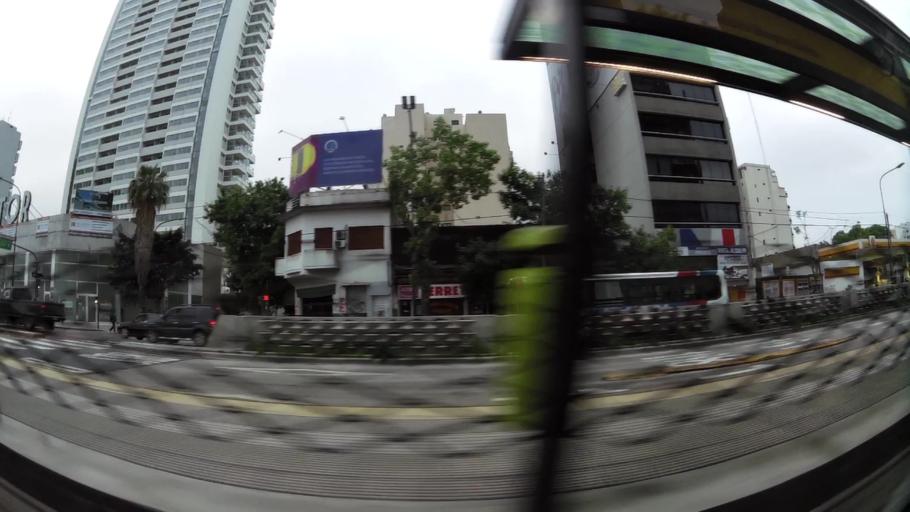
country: AR
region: Buenos Aires
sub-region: Partido de Vicente Lopez
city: Olivos
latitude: -34.5409
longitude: -58.4742
